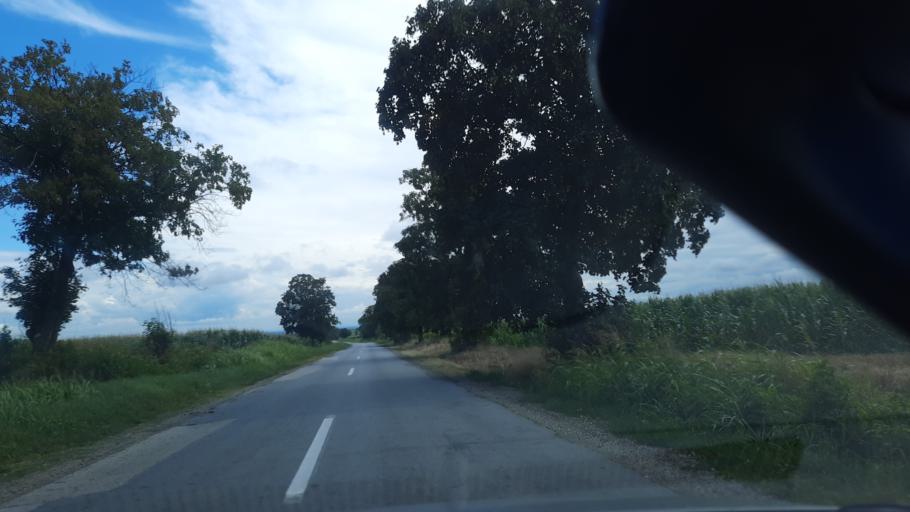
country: RS
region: Autonomna Pokrajina Vojvodina
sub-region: Sremski Okrug
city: Sremska Mitrovica
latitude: 45.1099
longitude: 19.5672
